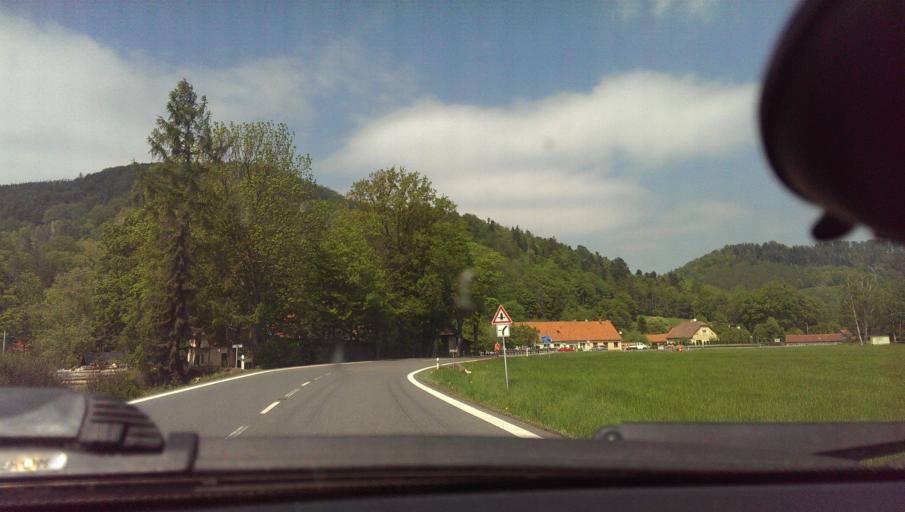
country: CZ
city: Lichnov (o. Novy Jicin)
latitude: 49.5728
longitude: 18.1828
